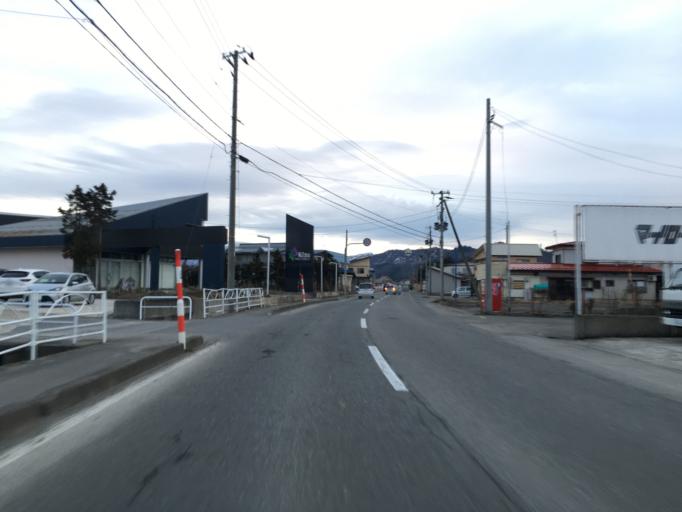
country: JP
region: Yamagata
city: Yonezawa
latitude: 37.9329
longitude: 140.0813
